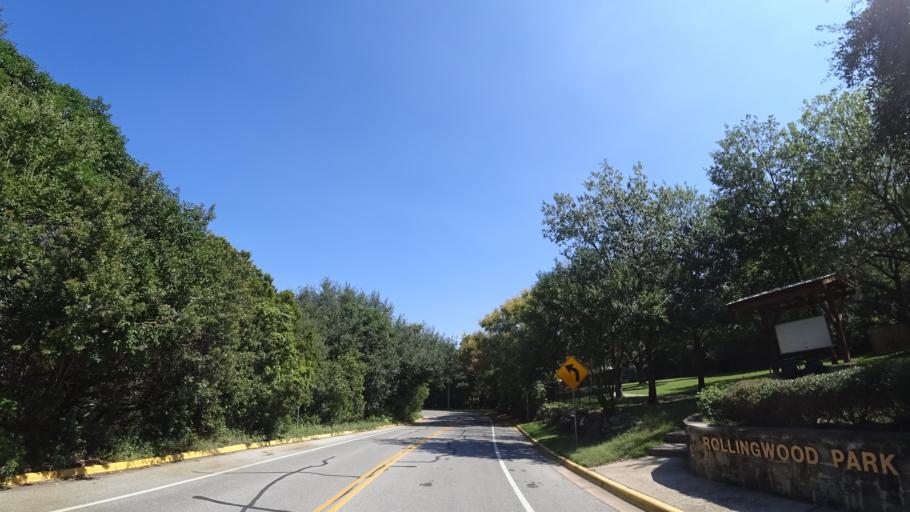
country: US
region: Texas
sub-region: Travis County
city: Rollingwood
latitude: 30.2760
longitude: -97.7886
